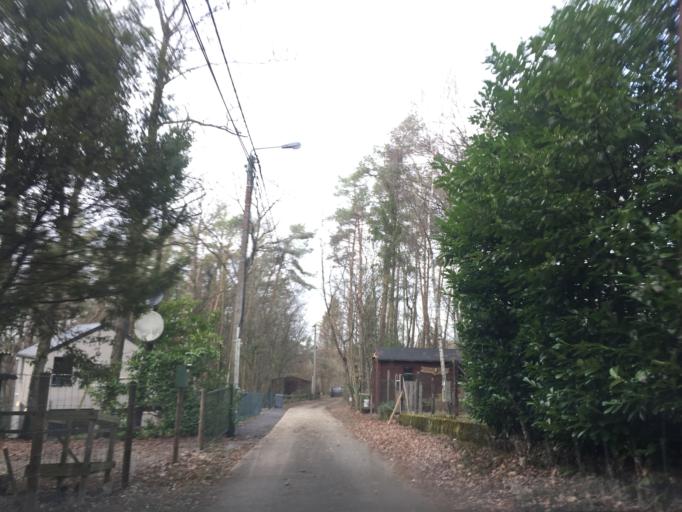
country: BE
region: Wallonia
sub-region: Province du Luxembourg
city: Hotton
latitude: 50.3013
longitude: 5.4954
